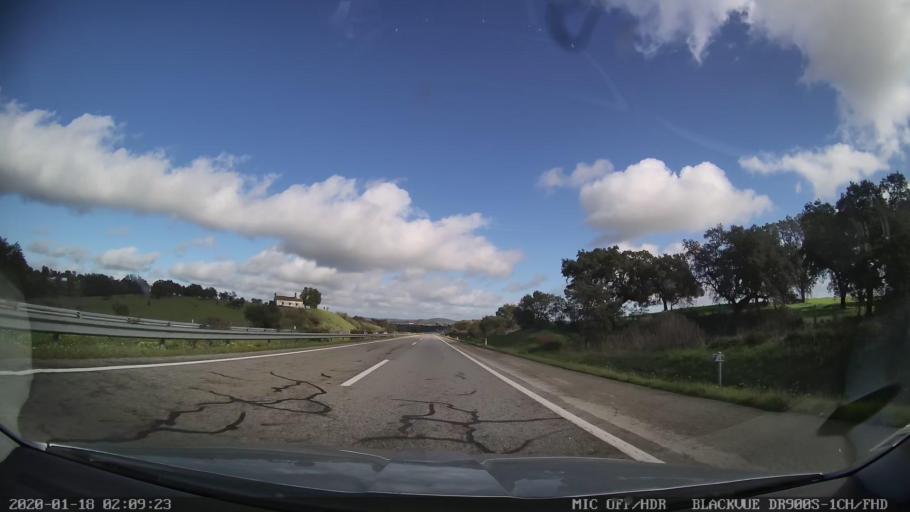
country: PT
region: Evora
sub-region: Montemor-O-Novo
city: Montemor-o-Novo
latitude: 38.6402
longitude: -8.2770
